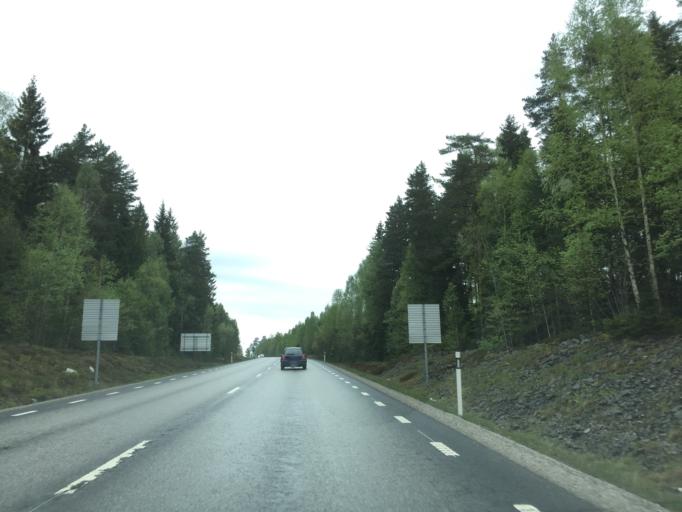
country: SE
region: OErebro
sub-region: Lindesbergs Kommun
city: Lindesberg
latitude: 59.5572
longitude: 15.2208
